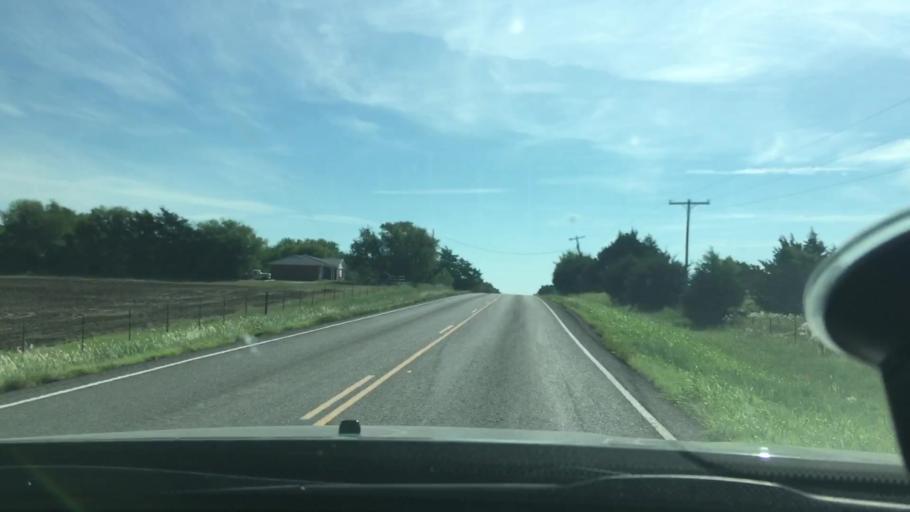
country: US
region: Oklahoma
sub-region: Carter County
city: Ardmore
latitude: 34.3327
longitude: -97.1837
